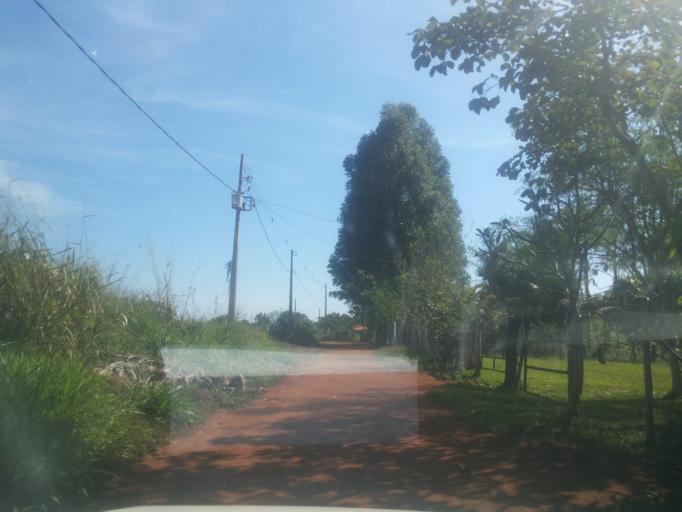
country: BR
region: Minas Gerais
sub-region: Santa Vitoria
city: Santa Vitoria
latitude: -18.9869
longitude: -50.3626
